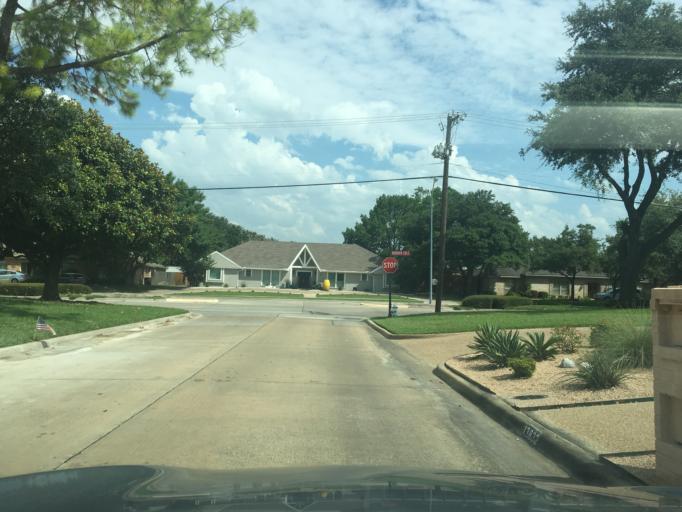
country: US
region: Texas
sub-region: Dallas County
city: Farmers Branch
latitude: 32.9325
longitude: -96.8591
